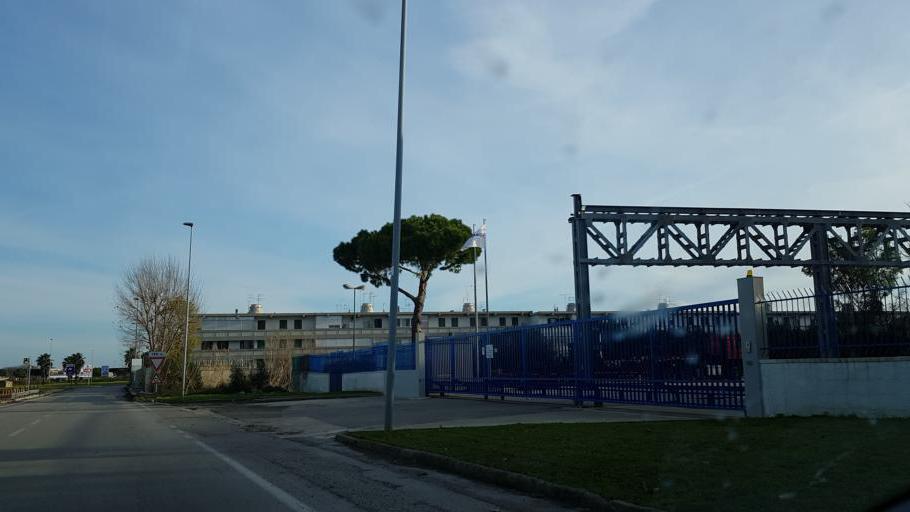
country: IT
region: Apulia
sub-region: Provincia di Brindisi
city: Brindisi
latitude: 40.6297
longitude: 17.9594
